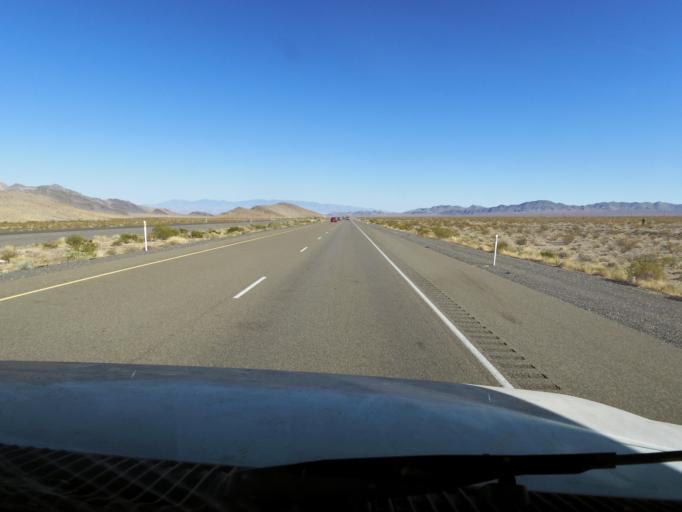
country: US
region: Nevada
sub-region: Nye County
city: Pahrump
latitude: 36.5718
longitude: -115.8705
